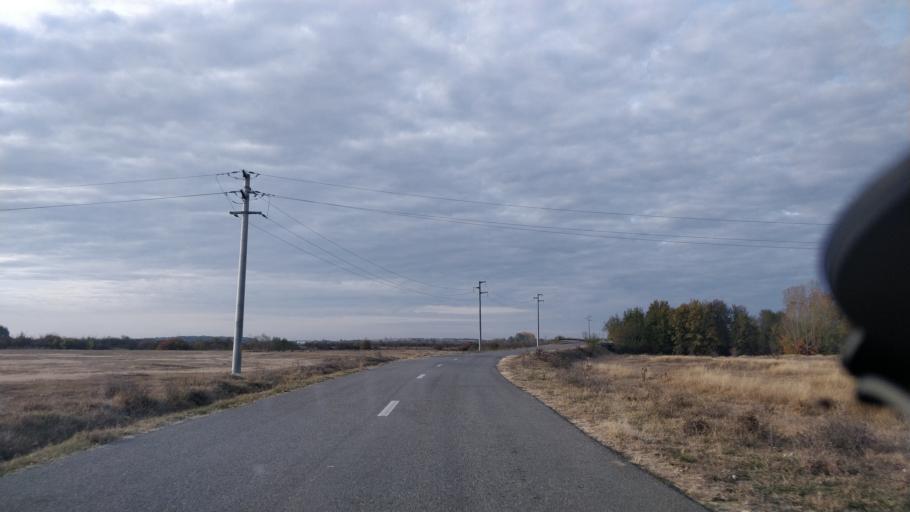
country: RO
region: Giurgiu
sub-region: Comuna Bucsani
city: Bucsani
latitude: 44.3398
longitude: 25.6621
